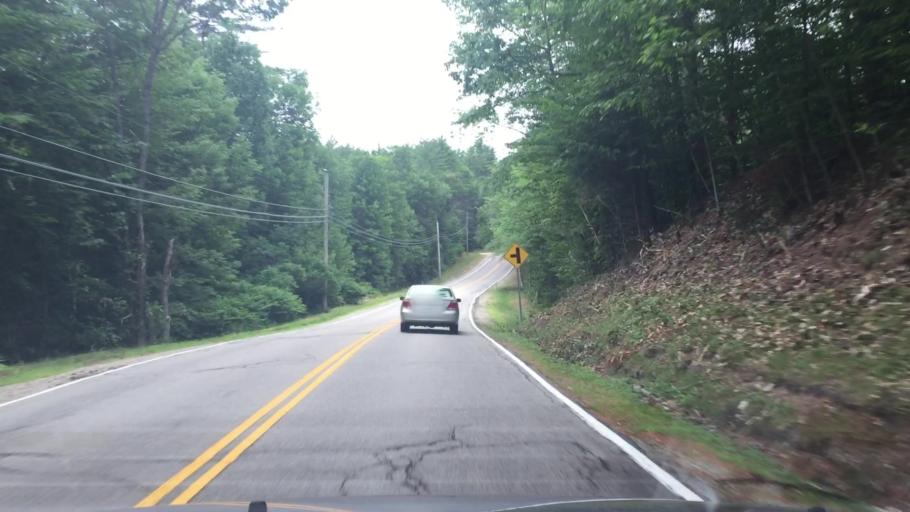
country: US
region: New Hampshire
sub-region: Carroll County
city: Conway
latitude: 43.9262
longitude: -71.0803
